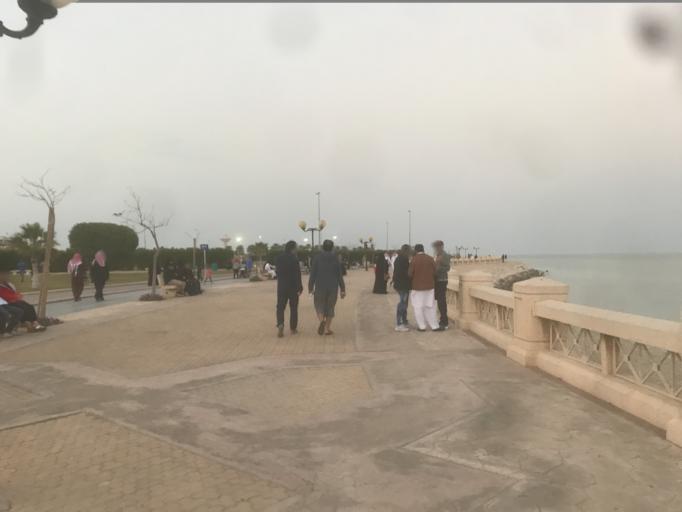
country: SA
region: Eastern Province
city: Khobar
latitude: 26.2894
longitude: 50.2227
